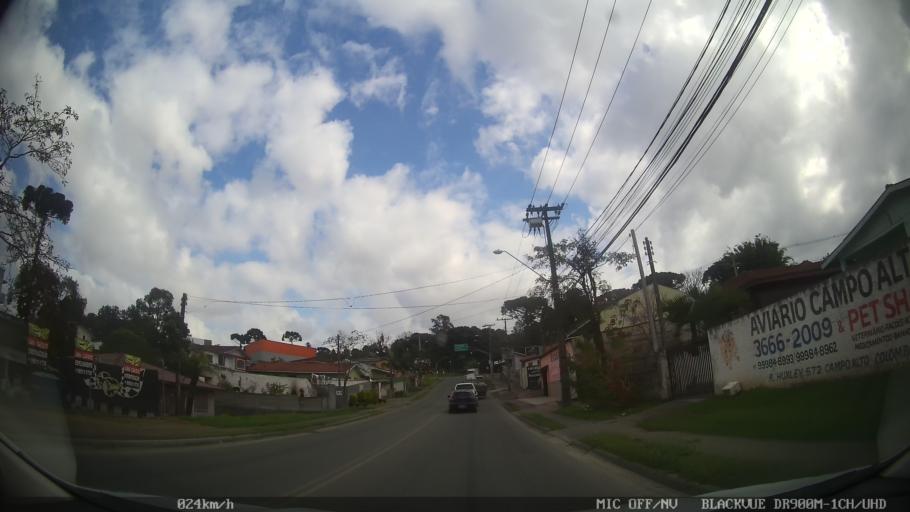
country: BR
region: Parana
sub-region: Colombo
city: Colombo
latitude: -25.3461
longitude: -49.1980
